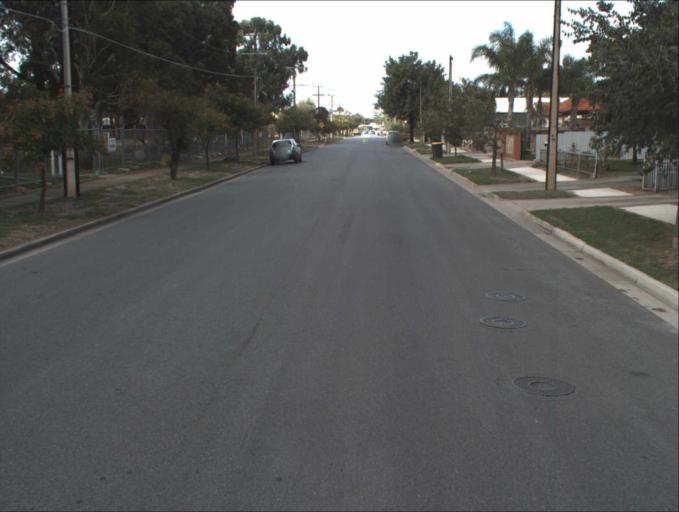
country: AU
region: South Australia
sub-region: Charles Sturt
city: Woodville
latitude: -34.8769
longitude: 138.5573
